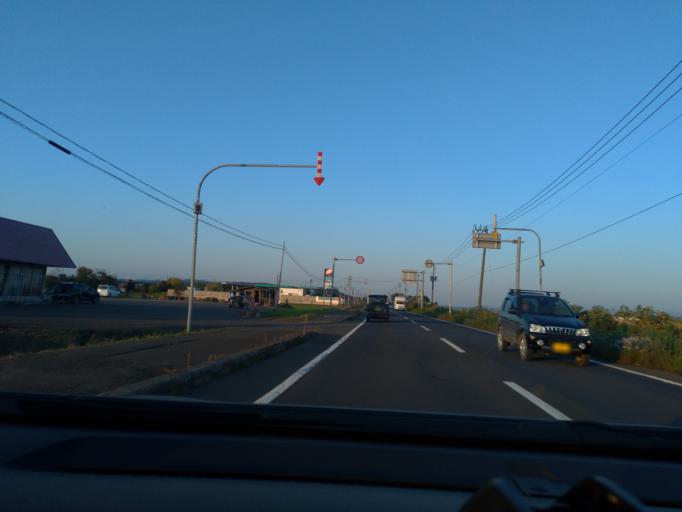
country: JP
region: Hokkaido
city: Tobetsu
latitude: 43.2163
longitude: 141.5312
